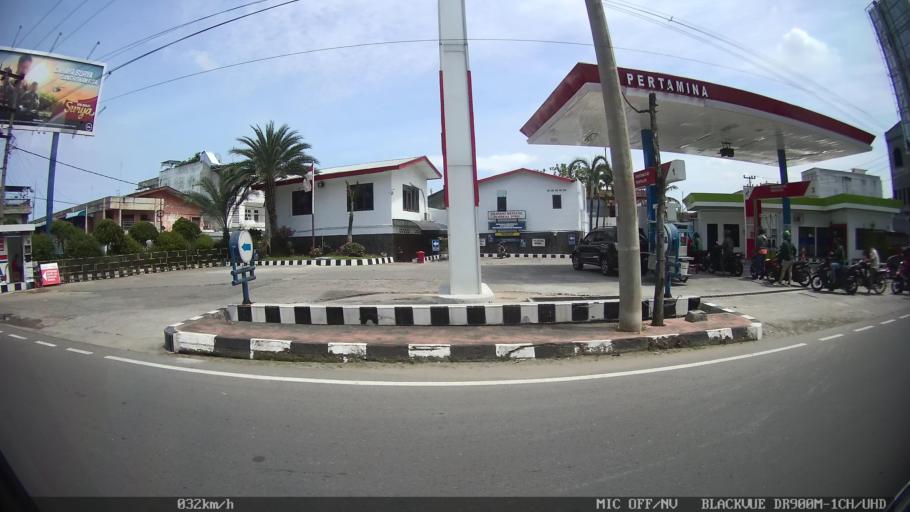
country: ID
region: North Sumatra
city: Medan
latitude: 3.5947
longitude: 98.6724
